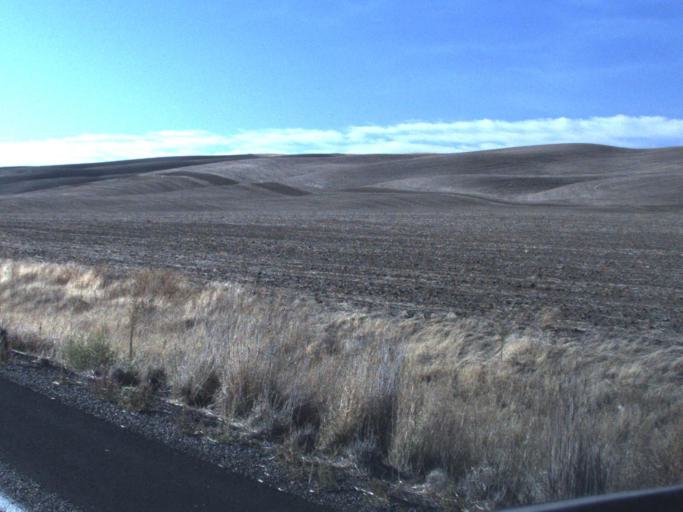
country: US
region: Washington
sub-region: Walla Walla County
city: Waitsburg
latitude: 46.2991
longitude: -118.3889
